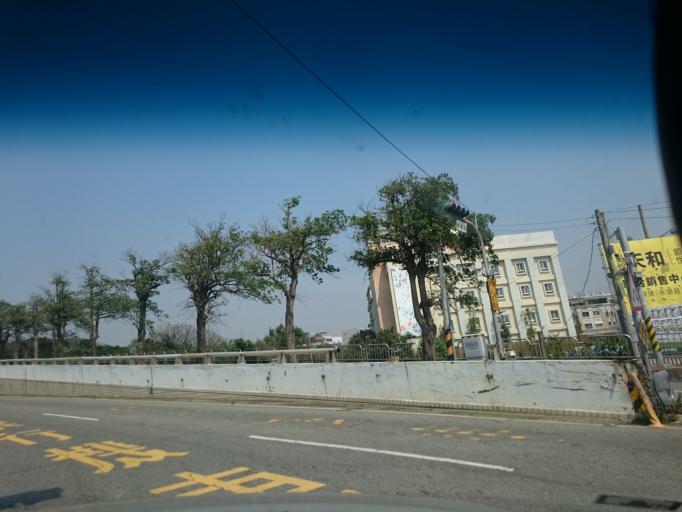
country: TW
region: Taiwan
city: Fengyuan
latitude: 24.2424
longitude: 120.5716
